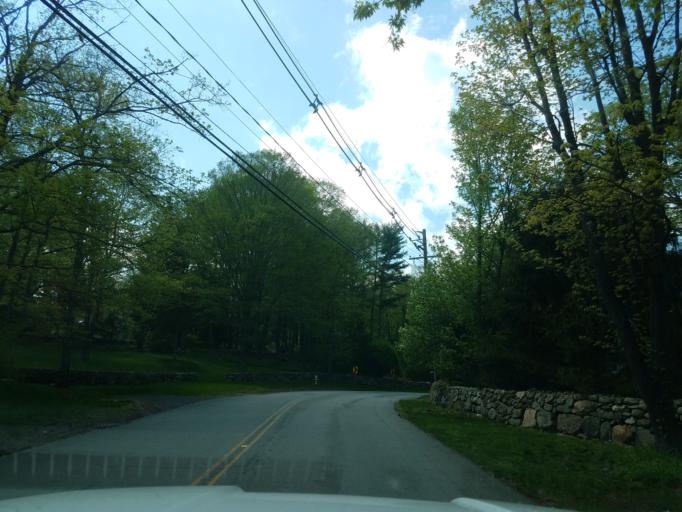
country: US
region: Connecticut
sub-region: Fairfield County
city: New Canaan
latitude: 41.1319
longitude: -73.4780
